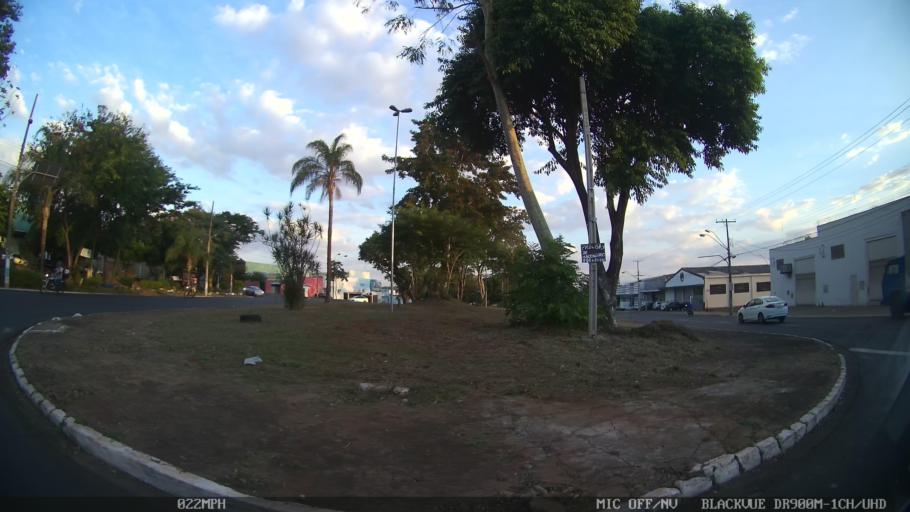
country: BR
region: Sao Paulo
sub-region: Ribeirao Preto
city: Ribeirao Preto
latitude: -21.1421
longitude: -47.7992
